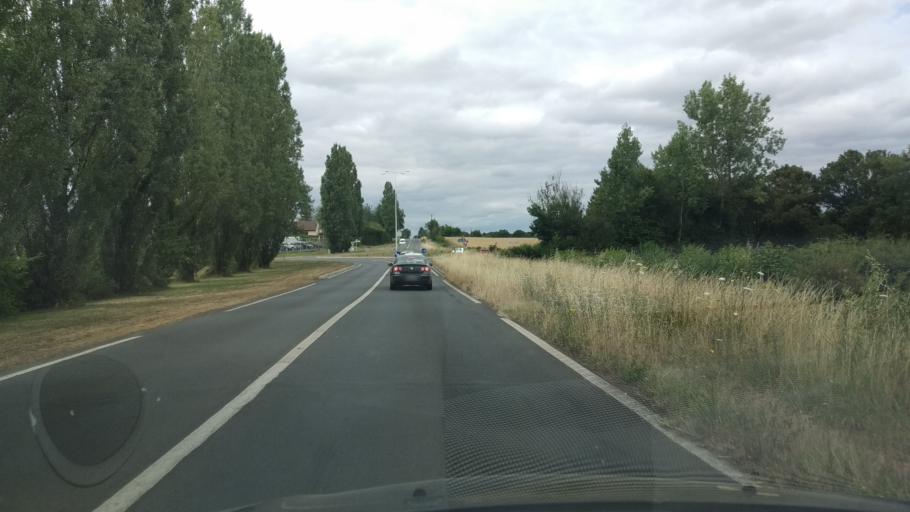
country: FR
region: Poitou-Charentes
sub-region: Departement de la Vienne
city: Smarves
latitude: 46.5044
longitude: 0.3622
